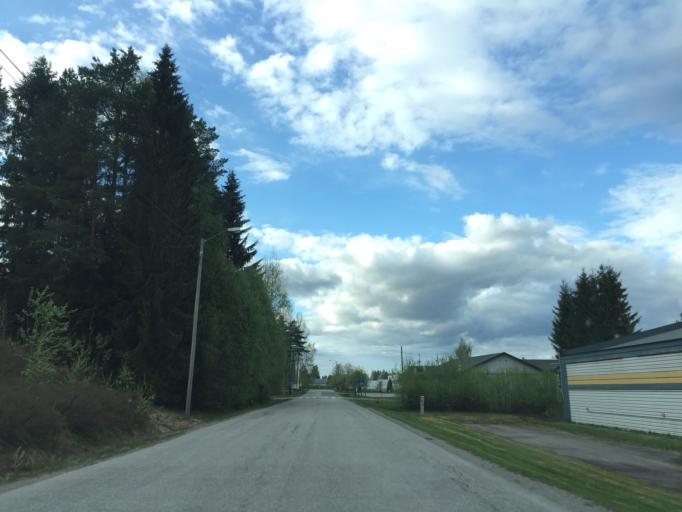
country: NO
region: Hedmark
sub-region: Kongsvinger
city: Kongsvinger
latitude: 60.1719
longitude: 12.0176
